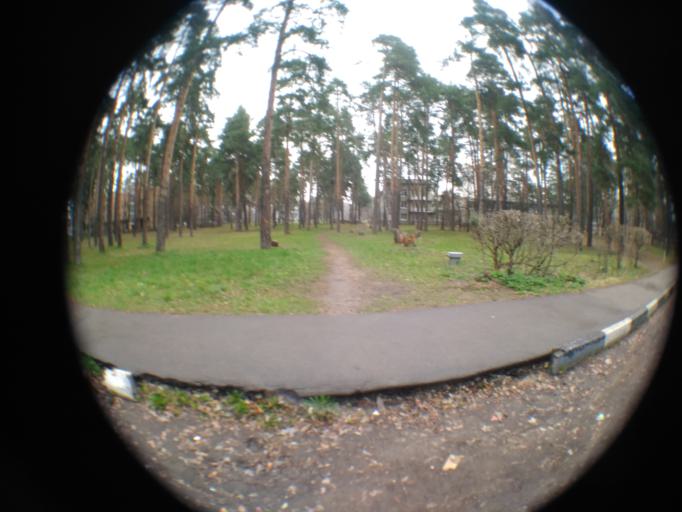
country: RU
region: Moskovskaya
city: Zhukovskiy
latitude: 55.5969
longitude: 38.1296
